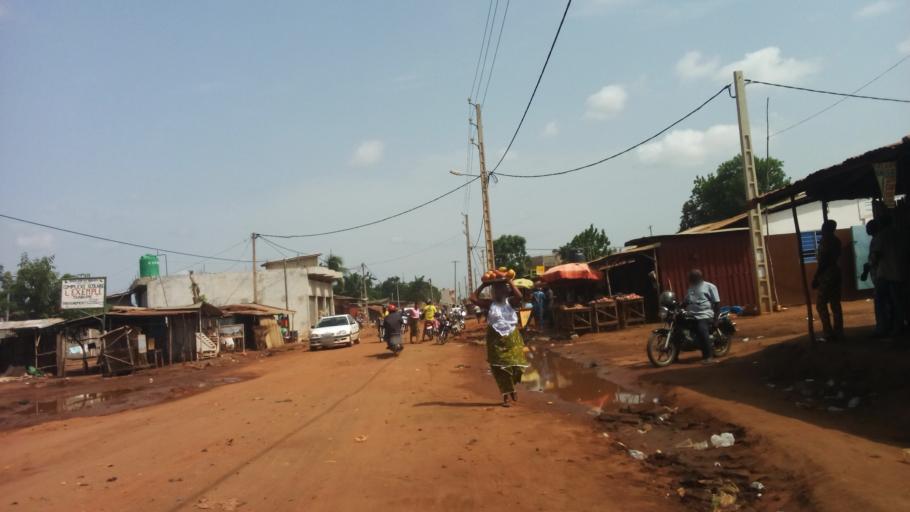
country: BJ
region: Atlantique
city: Abomey-Calavi
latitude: 6.4260
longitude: 2.3185
